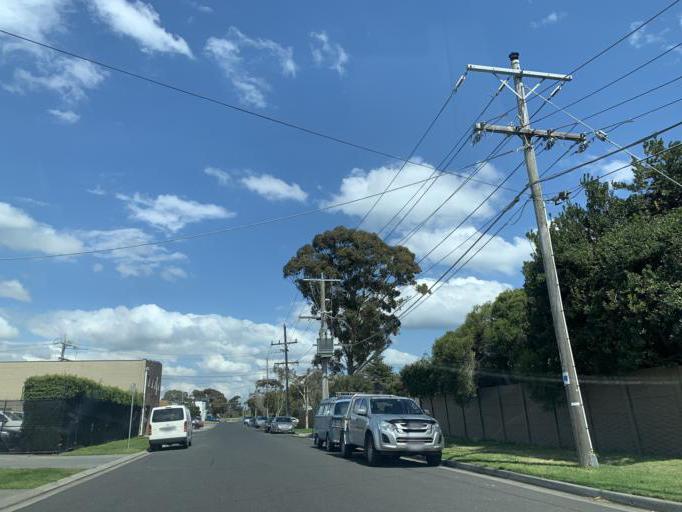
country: AU
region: Victoria
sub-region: Kingston
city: Mordialloc
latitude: -38.0068
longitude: 145.0953
